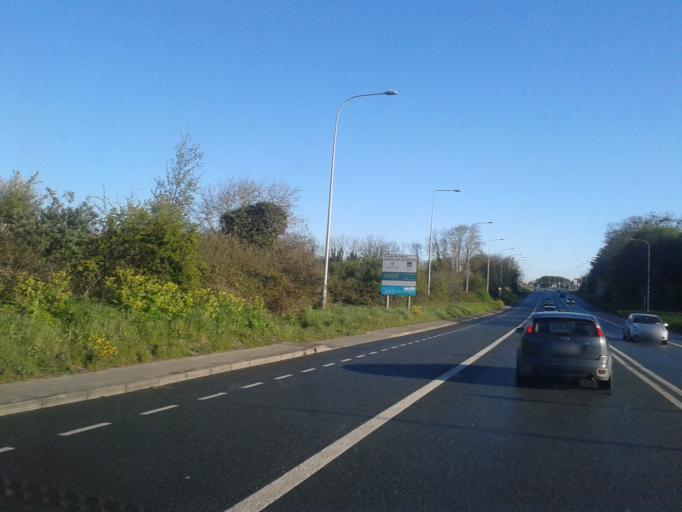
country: IE
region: Leinster
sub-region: Fingal County
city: Swords
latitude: 53.4379
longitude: -6.2275
